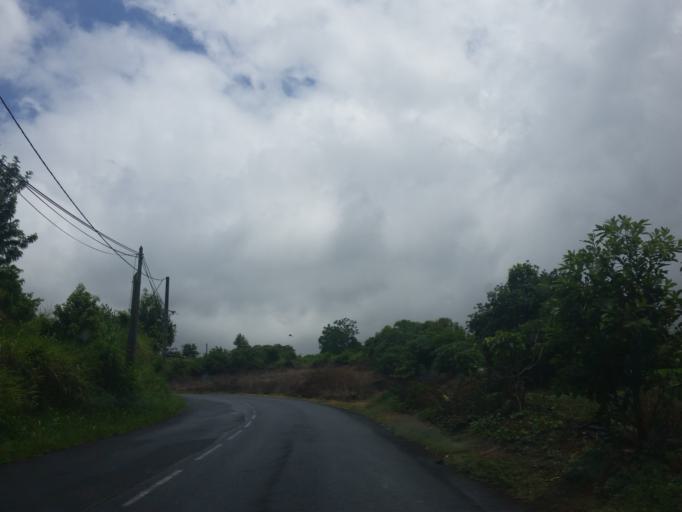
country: RE
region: Reunion
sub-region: Reunion
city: Le Tampon
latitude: -21.2531
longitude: 55.5028
